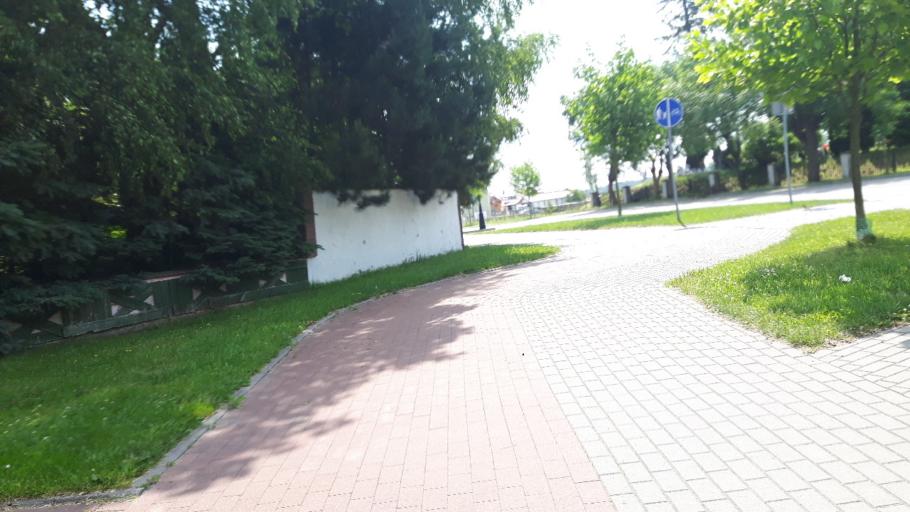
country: PL
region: Pomeranian Voivodeship
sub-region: Powiat leborski
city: Leba
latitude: 54.7506
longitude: 17.5630
